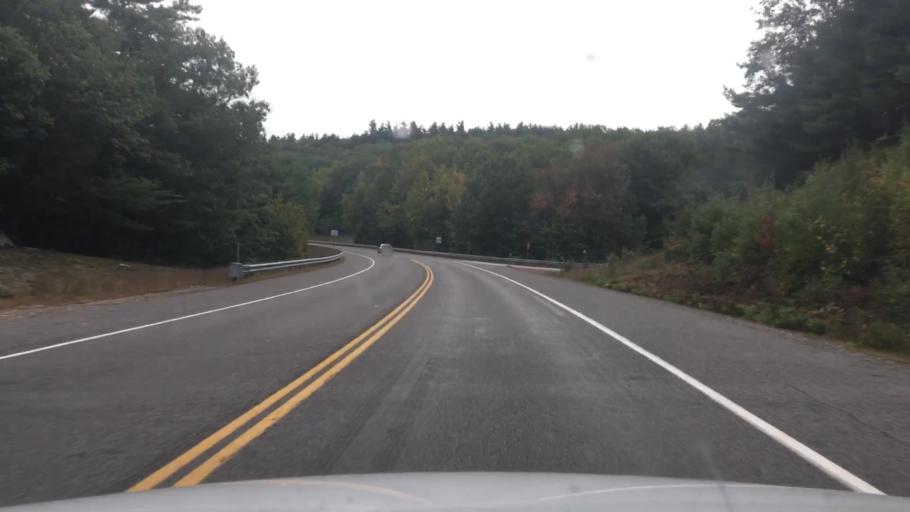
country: US
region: New Hampshire
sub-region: Carroll County
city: Wolfeboro
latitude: 43.5204
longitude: -71.2731
